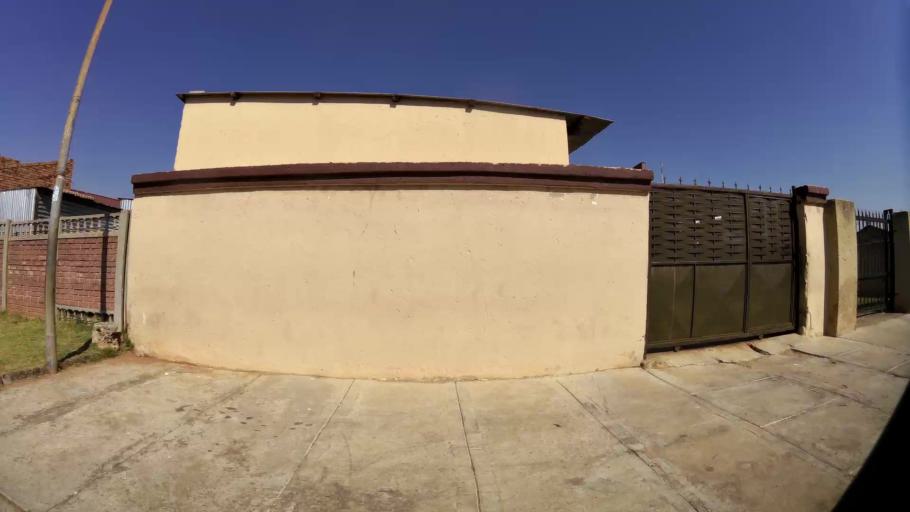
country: ZA
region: Gauteng
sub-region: City of Johannesburg Metropolitan Municipality
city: Soweto
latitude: -26.2415
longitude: 27.9518
